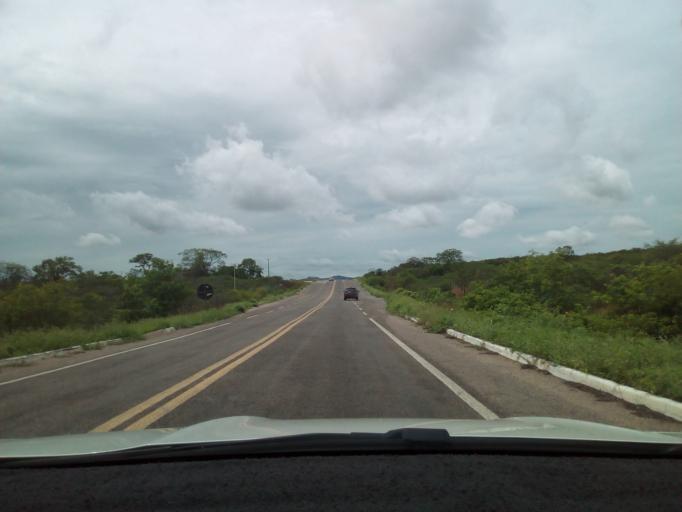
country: BR
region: Rio Grande do Norte
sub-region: Patu
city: Patu
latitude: -6.1478
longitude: -37.7499
